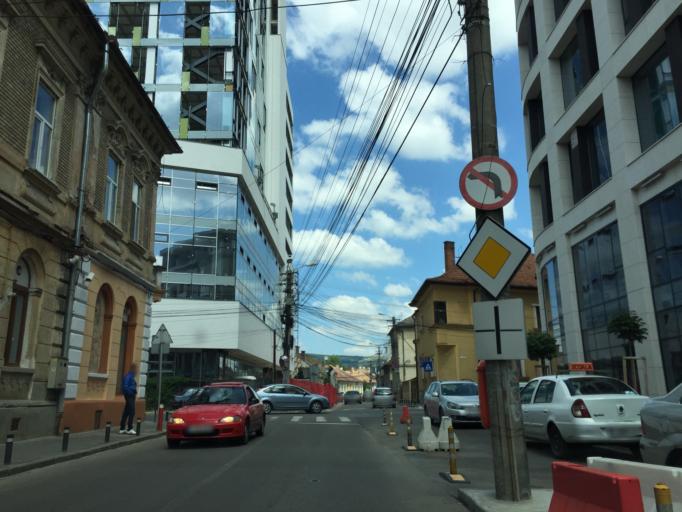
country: RO
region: Cluj
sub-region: Municipiul Cluj-Napoca
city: Cluj-Napoca
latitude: 46.7754
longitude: 23.5946
